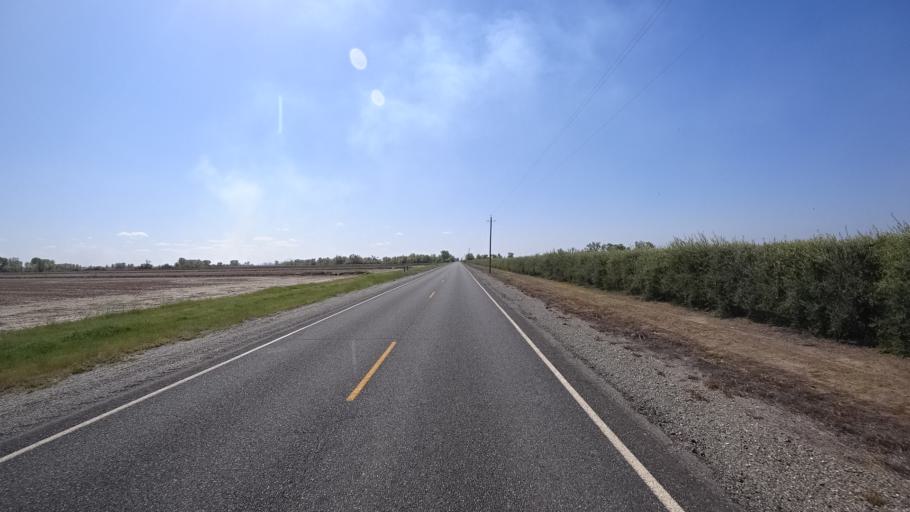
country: US
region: California
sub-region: Butte County
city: Durham
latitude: 39.4737
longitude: -121.9300
